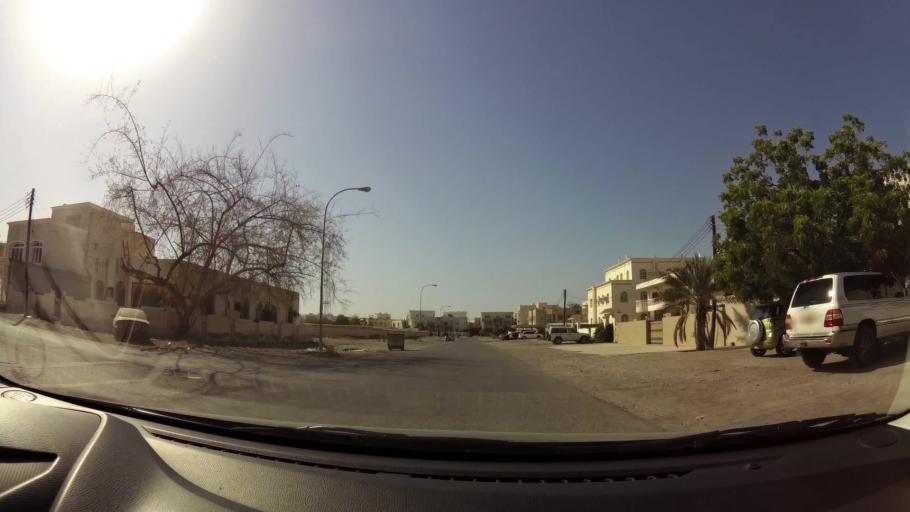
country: OM
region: Muhafazat Masqat
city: As Sib al Jadidah
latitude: 23.6310
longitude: 58.2045
